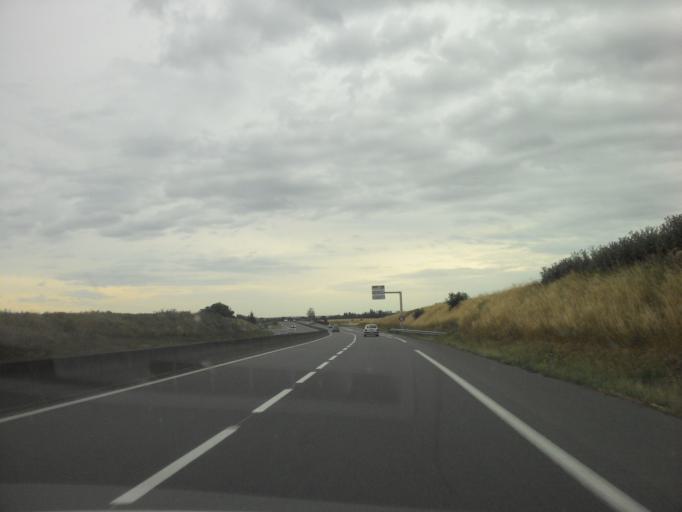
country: FR
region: Auvergne
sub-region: Departement du Puy-de-Dome
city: Menetrol
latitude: 45.8853
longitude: 3.1357
